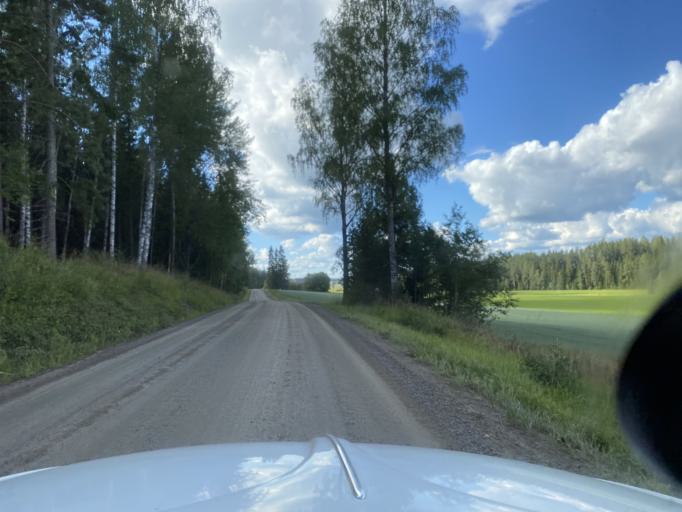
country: FI
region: Pirkanmaa
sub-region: Lounais-Pirkanmaa
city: Punkalaidun
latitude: 61.1221
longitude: 23.2655
